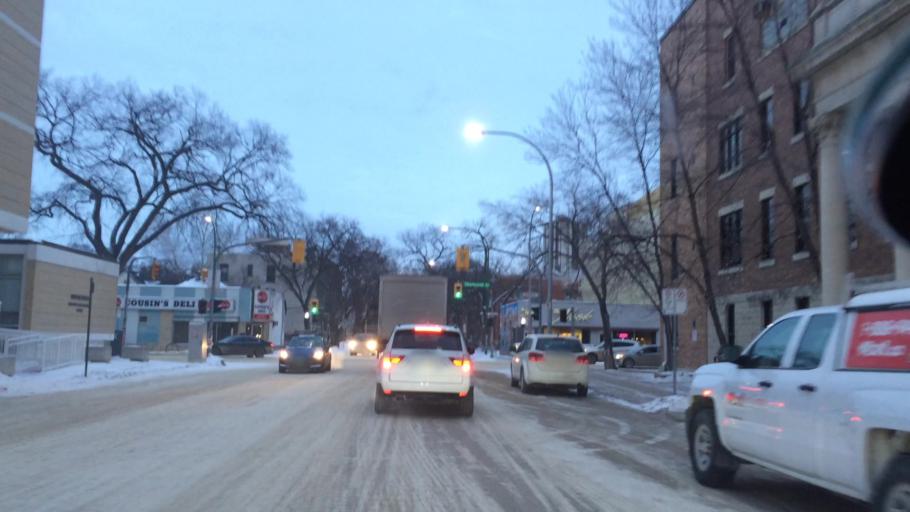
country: CA
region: Manitoba
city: Winnipeg
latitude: 49.8803
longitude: -97.1604
